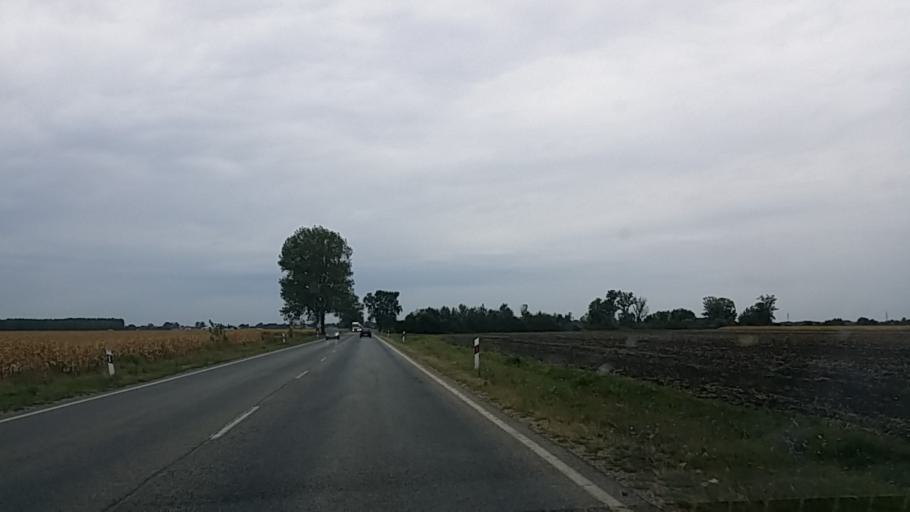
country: HU
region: Gyor-Moson-Sopron
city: Kapuvar
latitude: 47.5894
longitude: 17.0703
